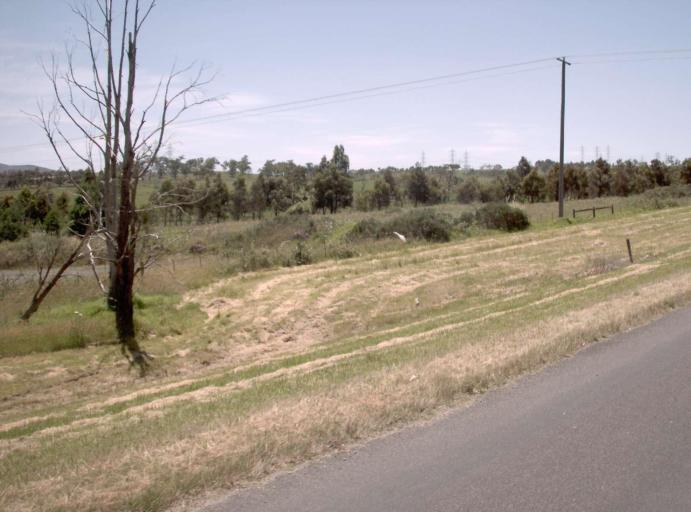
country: AU
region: Victoria
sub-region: Cardinia
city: Garfield
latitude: -38.0686
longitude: 145.6216
